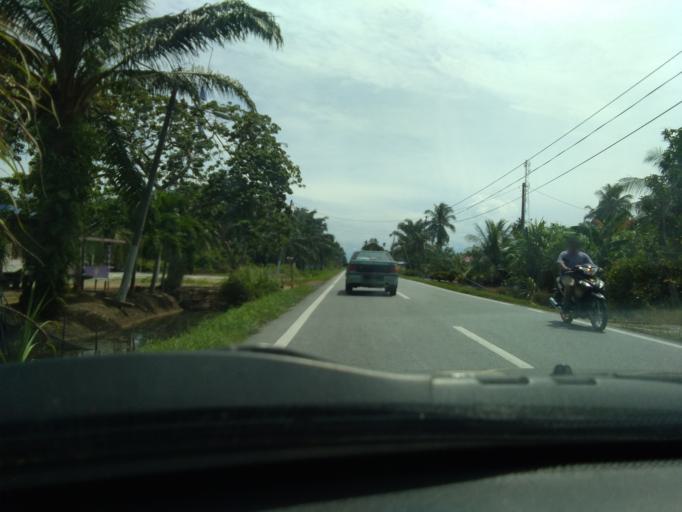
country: MY
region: Perak
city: Bagan Serai
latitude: 5.0339
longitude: 100.5648
